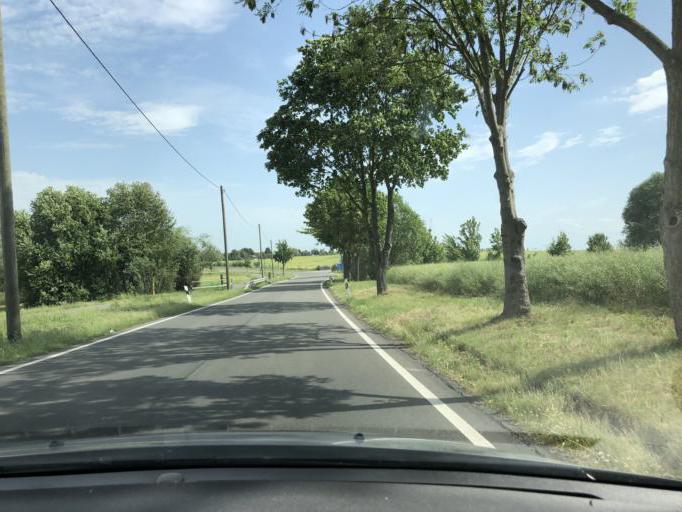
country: DE
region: Saxony
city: Taucha
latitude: 51.3741
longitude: 12.4992
